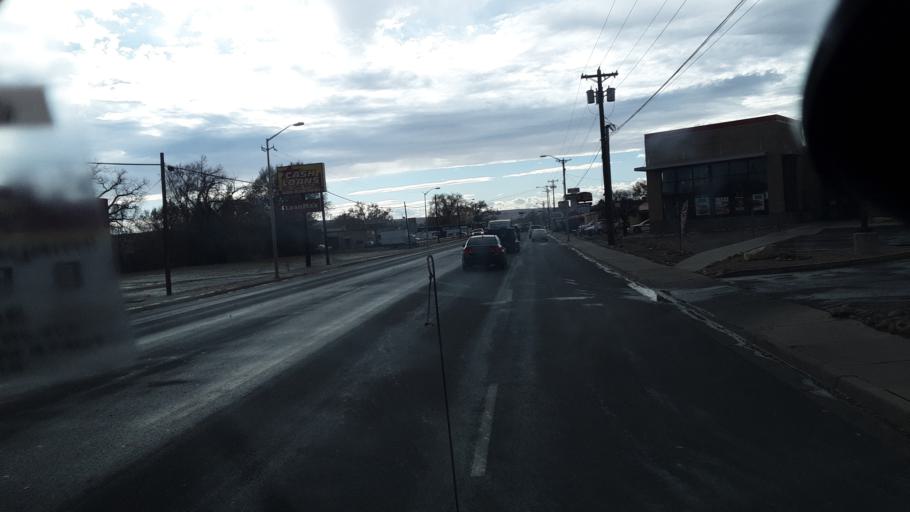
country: US
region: New Mexico
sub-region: San Juan County
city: Farmington
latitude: 36.7365
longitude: -108.1867
